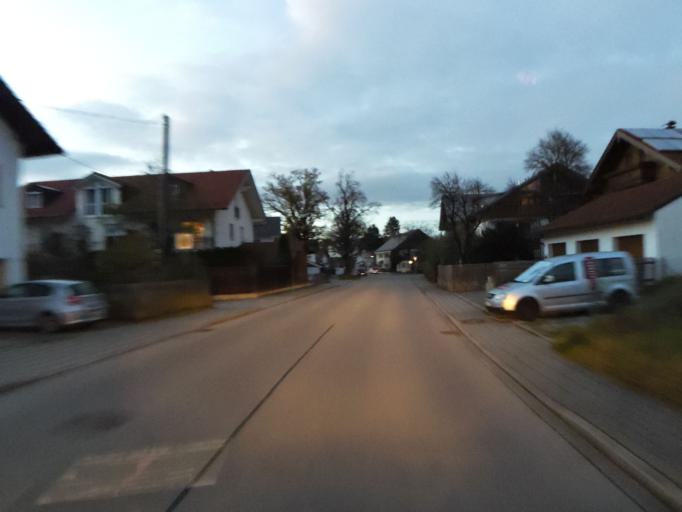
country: DE
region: Bavaria
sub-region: Upper Bavaria
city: Hohenkirchen-Siegertsbrunn
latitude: 47.9851
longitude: 11.7153
